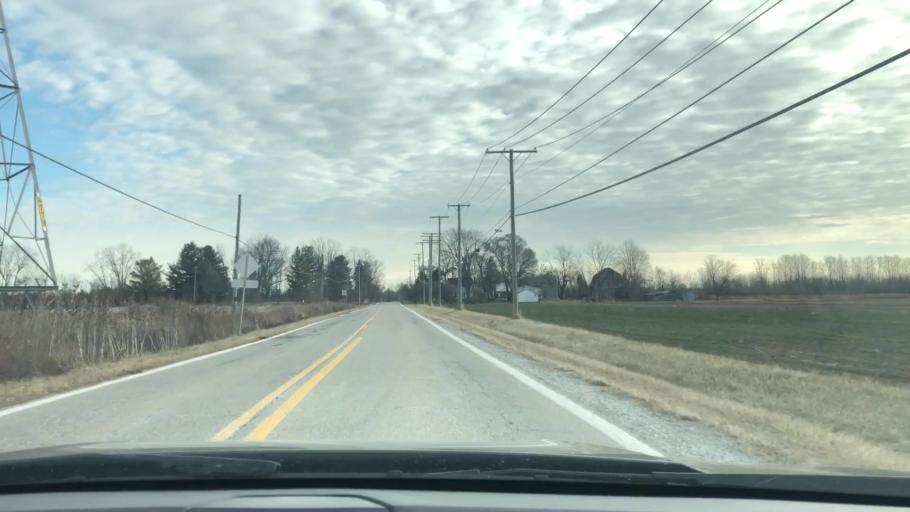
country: US
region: Michigan
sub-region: Macomb County
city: Shelby
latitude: 42.7293
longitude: -82.9955
